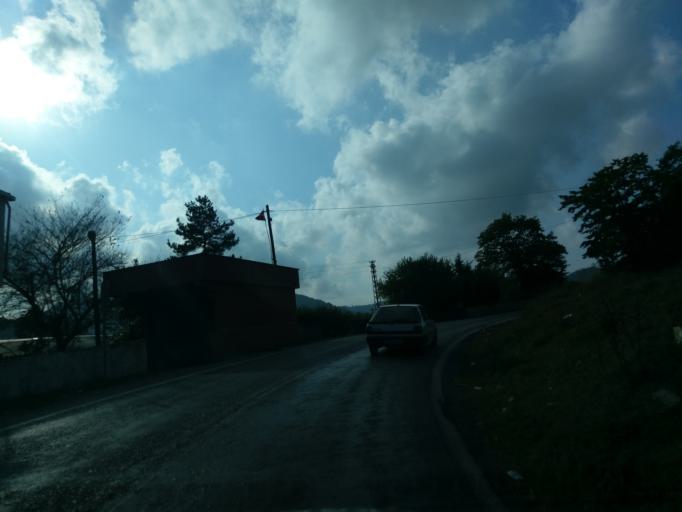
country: TR
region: Sinop
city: Helaldi
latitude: 41.9155
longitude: 34.4200
